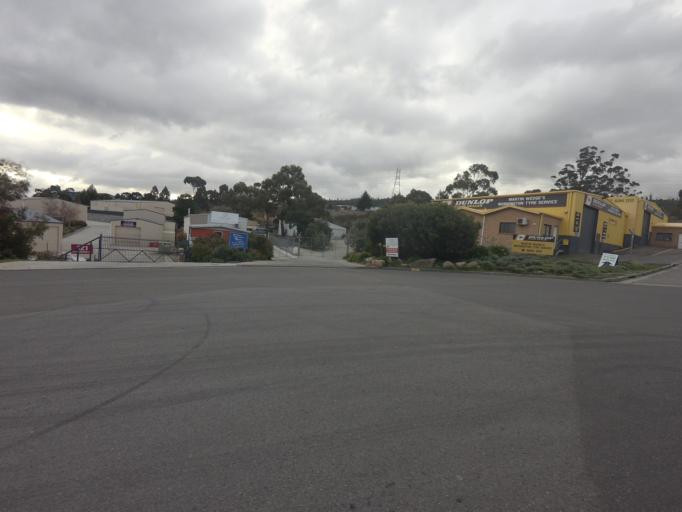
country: AU
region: Tasmania
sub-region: Clarence
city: Warrane
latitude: -42.8605
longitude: 147.4035
